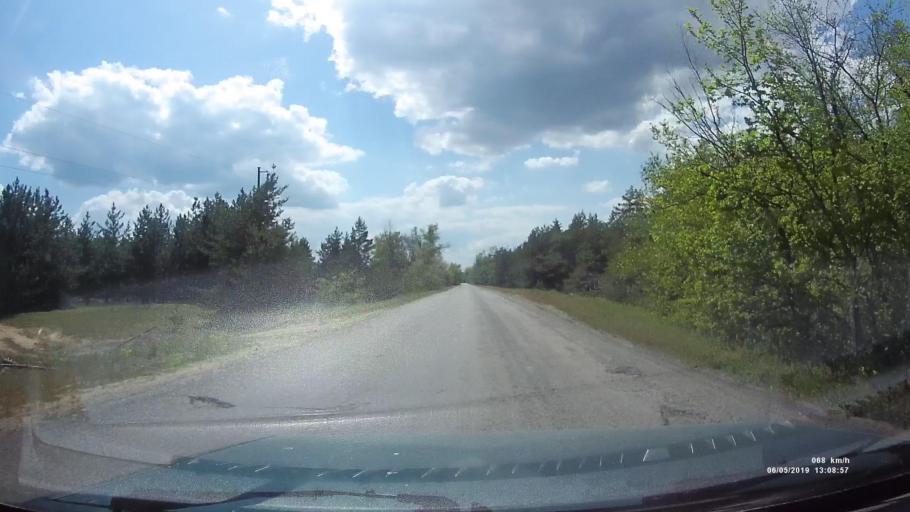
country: RU
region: Rostov
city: Ust'-Donetskiy
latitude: 47.7721
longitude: 40.9898
